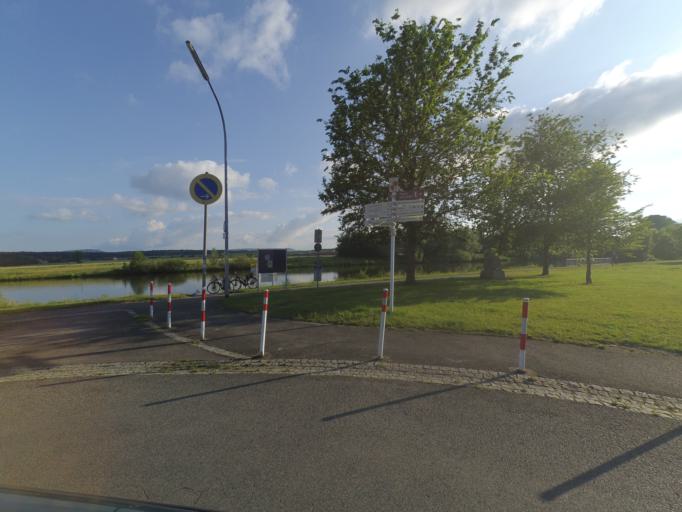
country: DE
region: Bavaria
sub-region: Regierungsbezirk Unterfranken
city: Hassfurt
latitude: 50.0300
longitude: 10.5101
